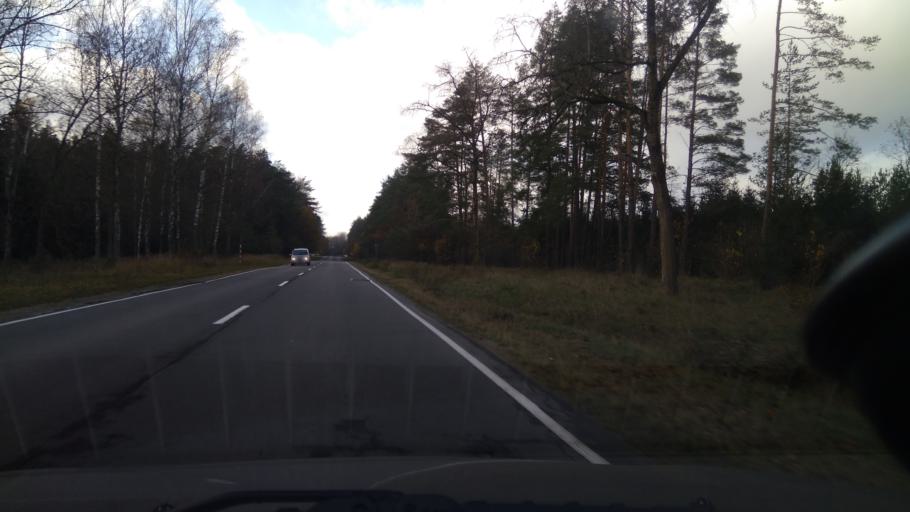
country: BY
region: Minsk
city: Slutsk
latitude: 53.2318
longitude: 27.6492
